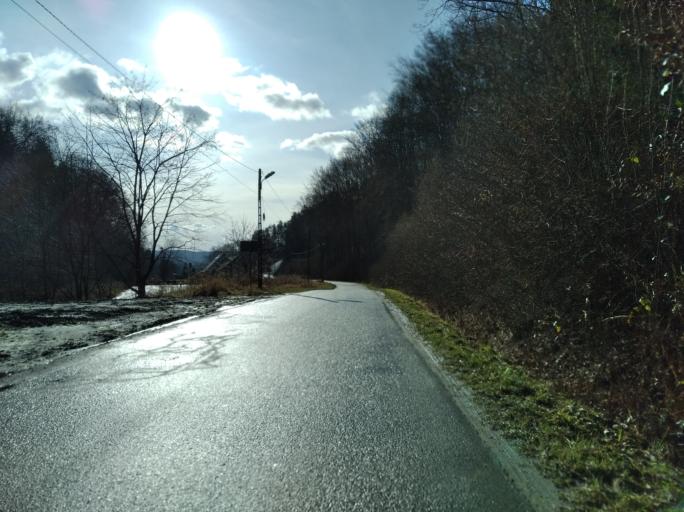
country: PL
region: Subcarpathian Voivodeship
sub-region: Powiat strzyzowski
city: Strzyzow
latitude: 49.8851
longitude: 21.7748
